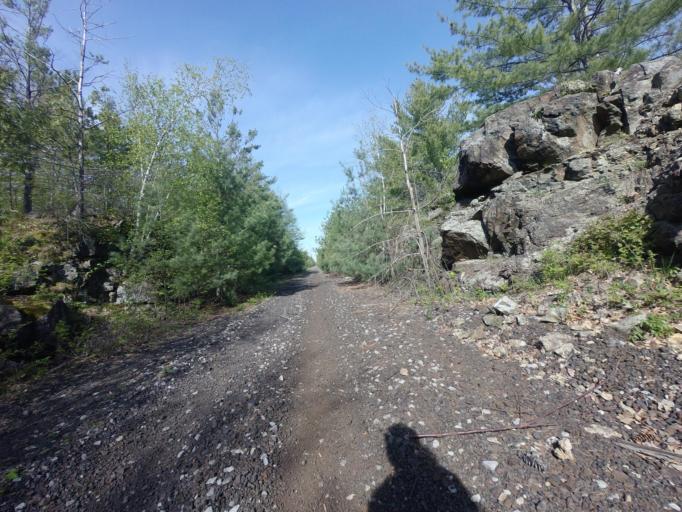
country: CA
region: Ontario
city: Arnprior
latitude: 45.4710
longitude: -76.2975
